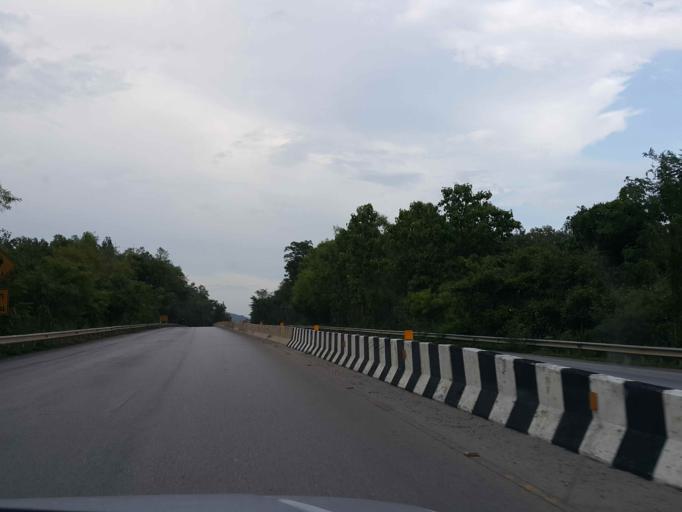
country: TH
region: Lampang
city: Soem Ngam
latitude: 18.0408
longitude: 99.3792
